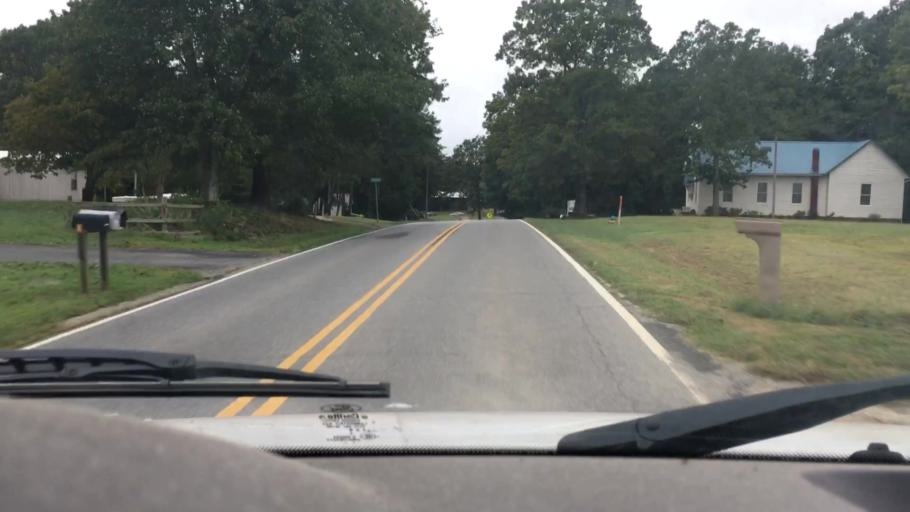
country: US
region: North Carolina
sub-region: Lincoln County
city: Denver
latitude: 35.5399
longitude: -81.0211
